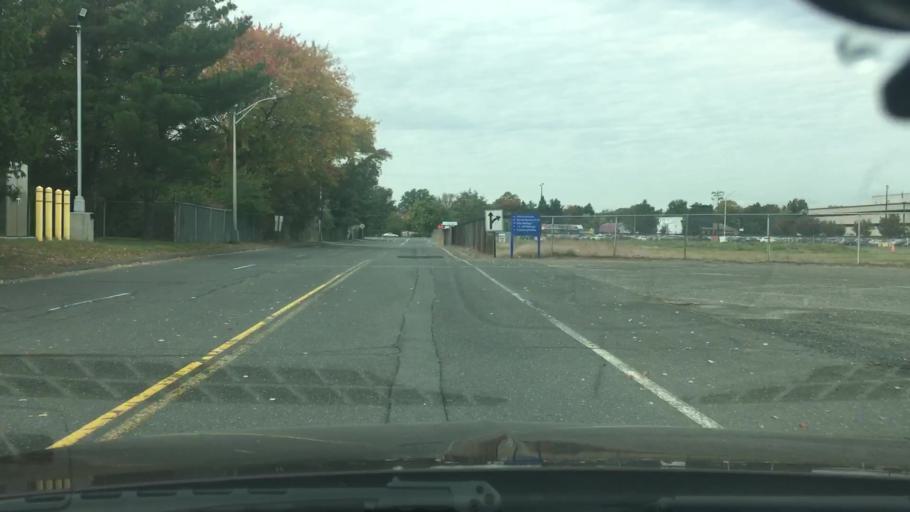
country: US
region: Connecticut
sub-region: Hartford County
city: Glastonbury
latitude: 41.7442
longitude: -72.6284
